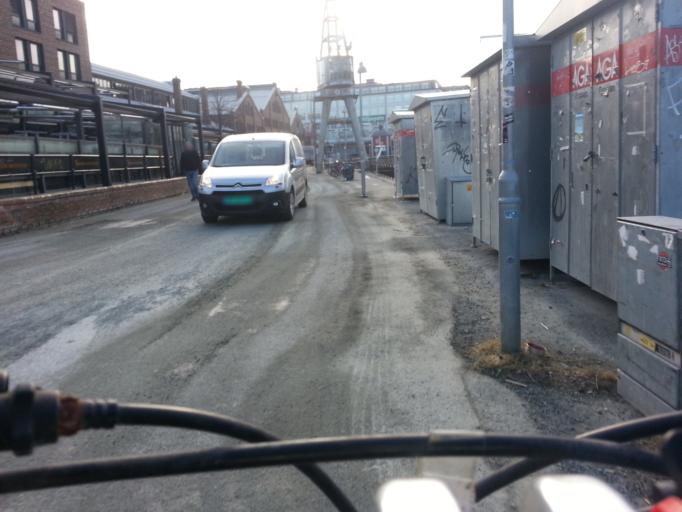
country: NO
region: Sor-Trondelag
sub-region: Trondheim
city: Trondheim
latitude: 63.4349
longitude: 10.4103
